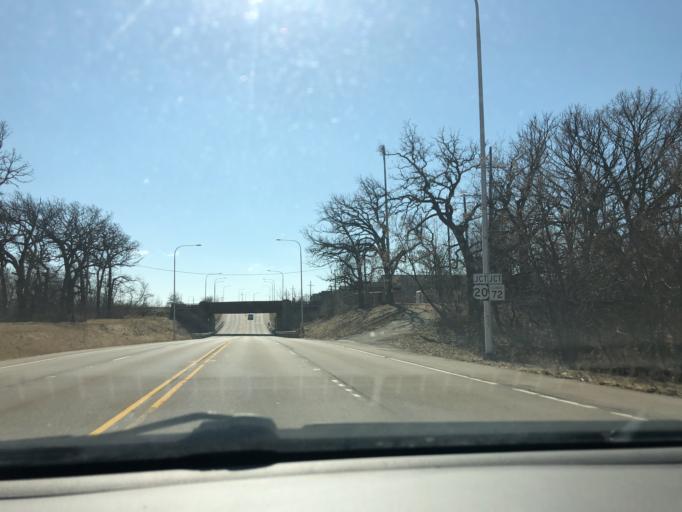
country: US
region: Illinois
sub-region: Kane County
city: Pingree Grove
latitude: 42.0859
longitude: -88.4563
